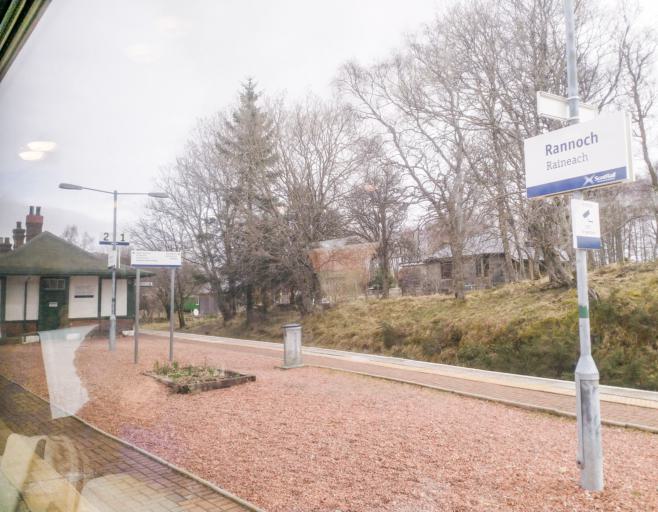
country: GB
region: Scotland
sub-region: Highland
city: Spean Bridge
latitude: 56.6856
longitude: -4.5772
